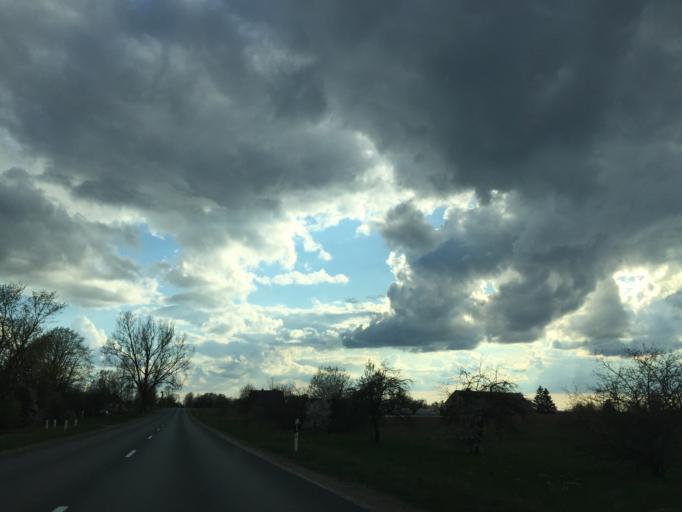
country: LV
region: Cesu Rajons
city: Cesis
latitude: 57.3255
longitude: 25.3028
